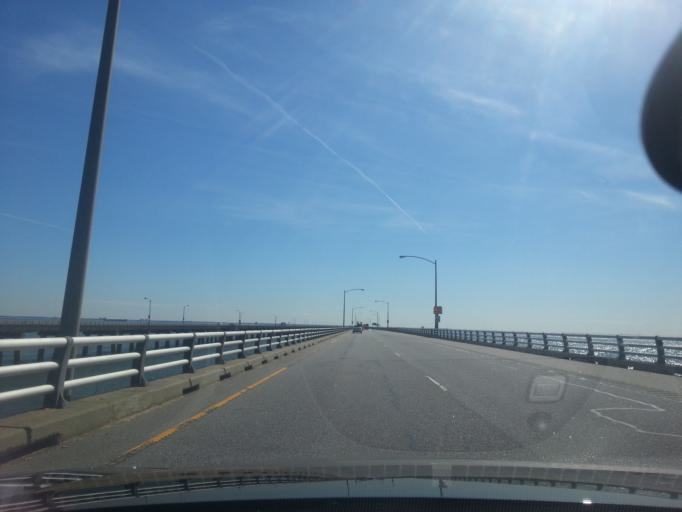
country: US
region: Virginia
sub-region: City of Virginia Beach
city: Virginia Beach
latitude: 37.0136
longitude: -76.0939
